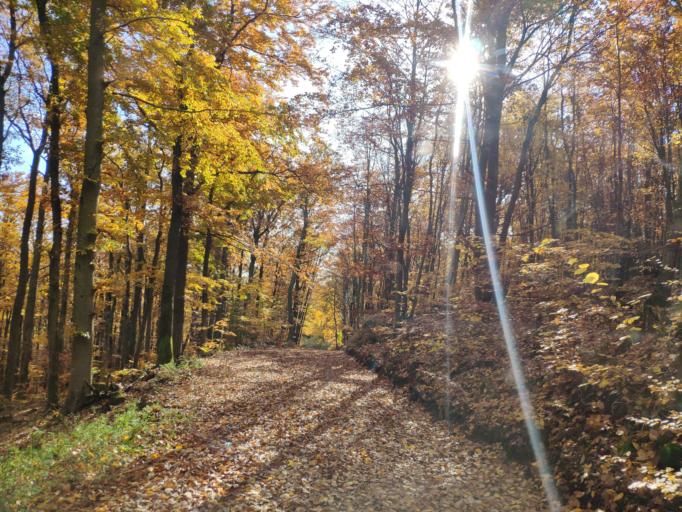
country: SK
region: Kosicky
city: Moldava nad Bodvou
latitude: 48.7239
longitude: 21.0349
